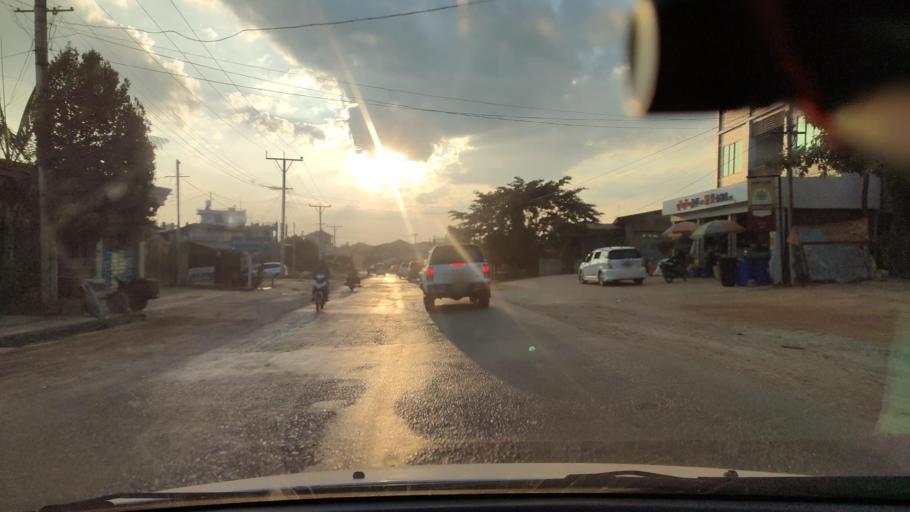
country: MM
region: Shan
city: Lashio
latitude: 22.7744
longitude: 97.6436
